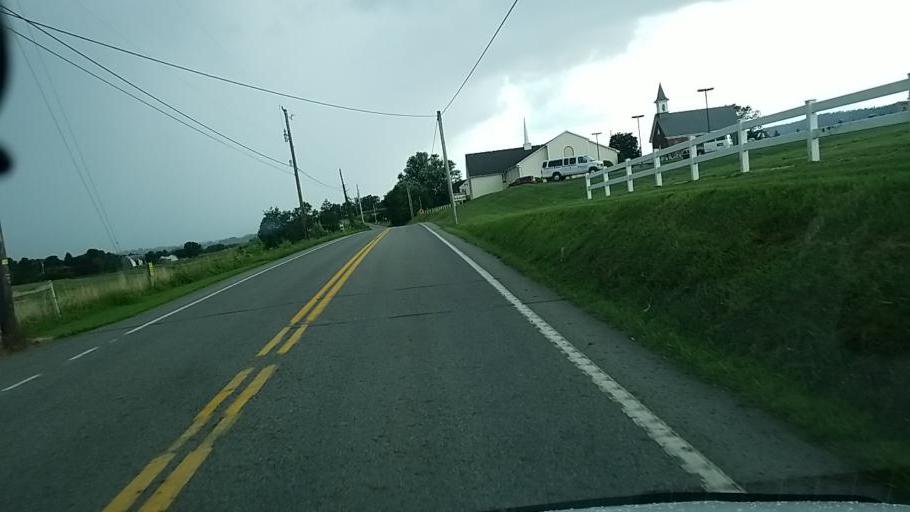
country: US
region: Pennsylvania
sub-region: Dauphin County
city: Elizabethville
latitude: 40.5819
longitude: -76.8730
